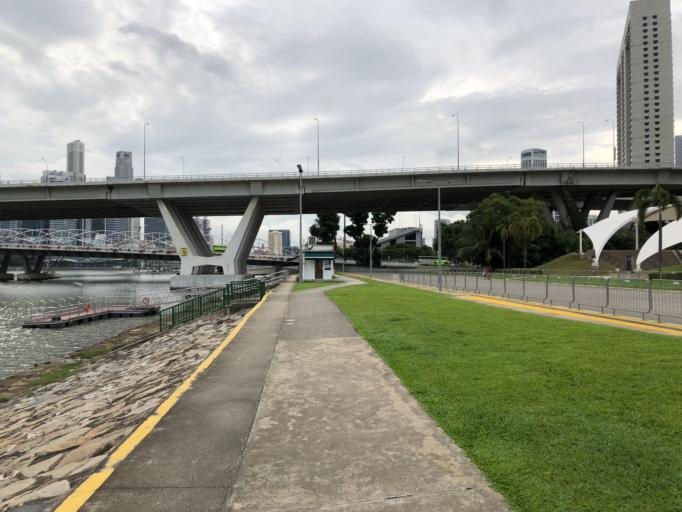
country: SG
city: Singapore
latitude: 1.2886
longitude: 103.8629
